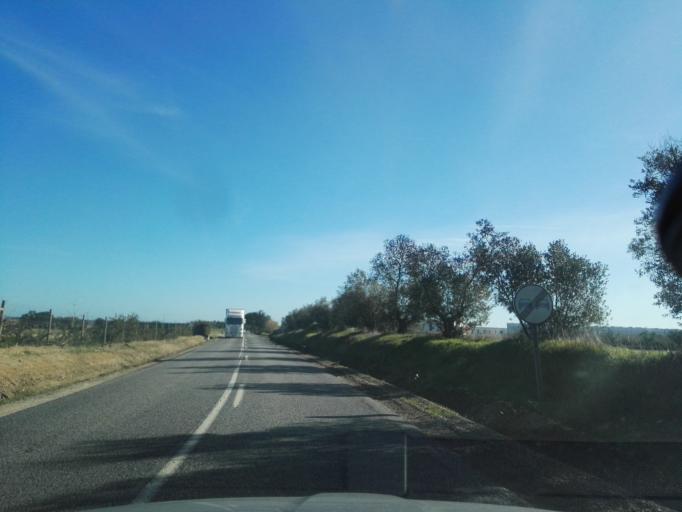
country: PT
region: Setubal
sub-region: Alcochete
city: Alcochete
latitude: 38.7284
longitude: -8.9178
